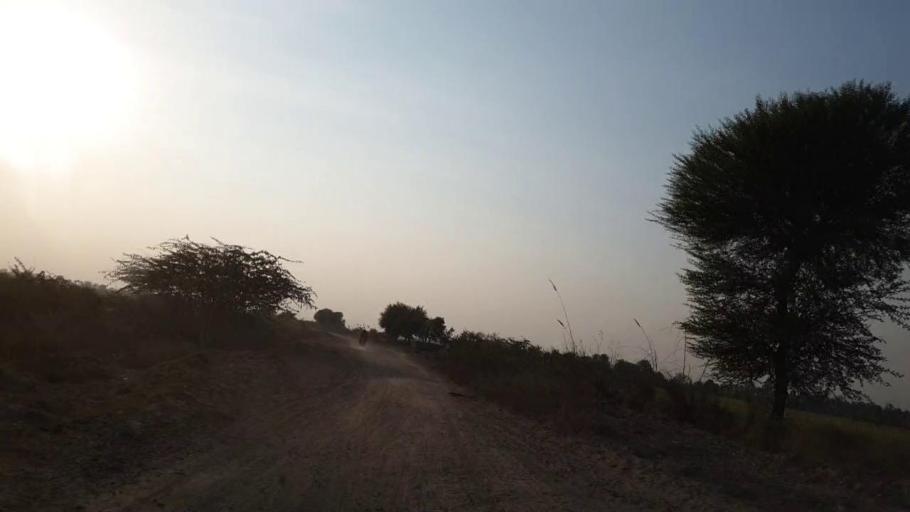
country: PK
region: Sindh
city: Pithoro
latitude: 25.6543
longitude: 69.2221
